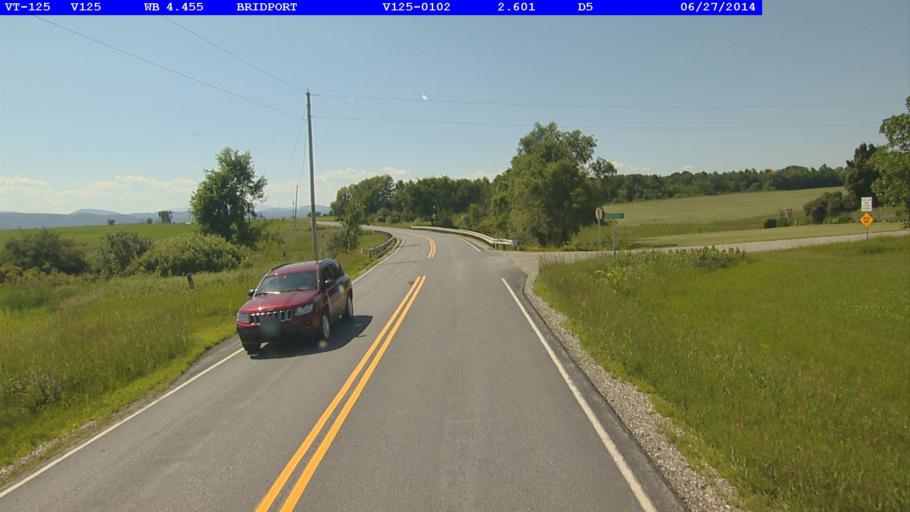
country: US
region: New York
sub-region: Essex County
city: Port Henry
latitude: 44.0000
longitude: -73.3575
